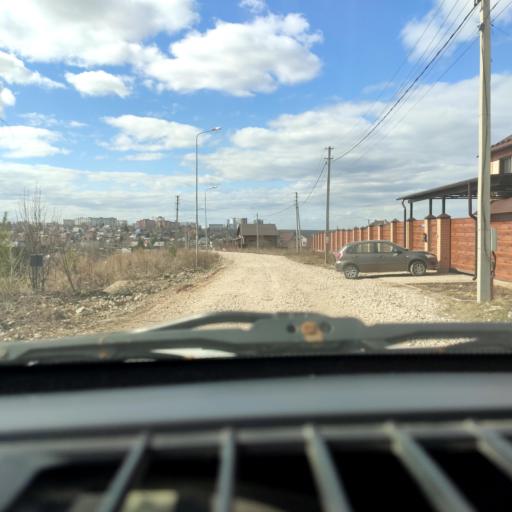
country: RU
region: Perm
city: Perm
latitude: 58.0243
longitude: 56.3502
